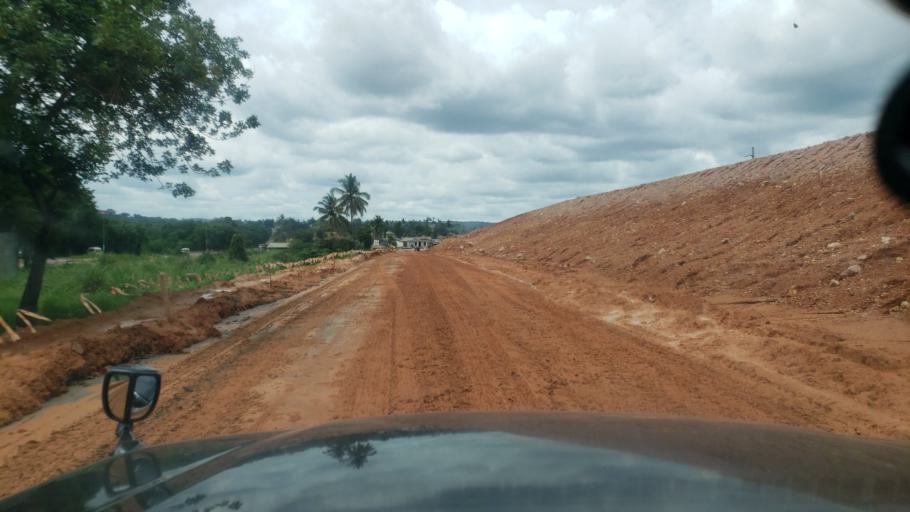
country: TZ
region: Pwani
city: Kisarawe
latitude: -6.8849
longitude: 39.1487
